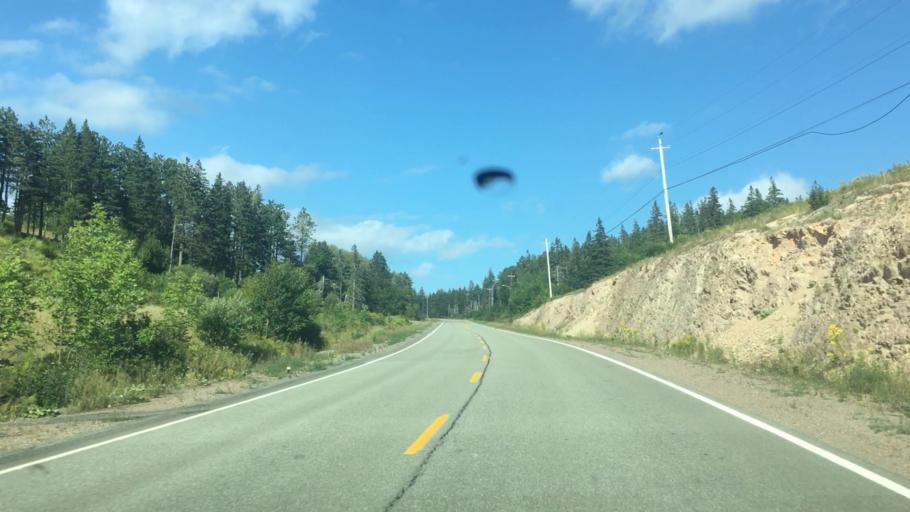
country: CA
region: Nova Scotia
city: Sydney
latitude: 45.8520
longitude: -60.6345
